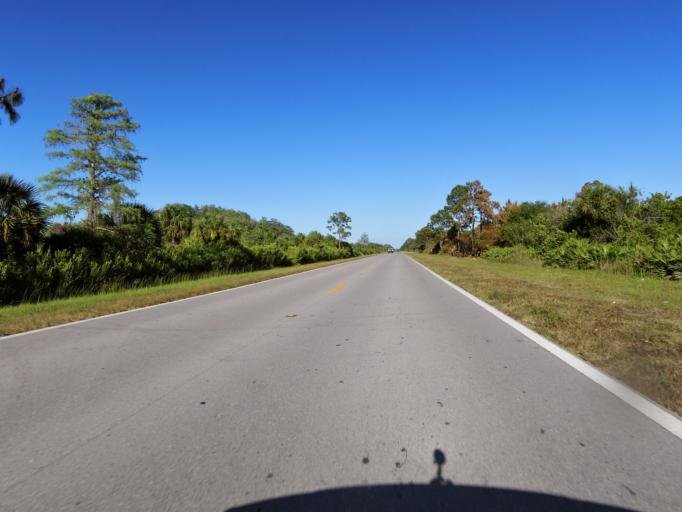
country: US
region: Florida
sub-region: Collier County
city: Immokalee
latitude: 26.2951
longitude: -81.4037
